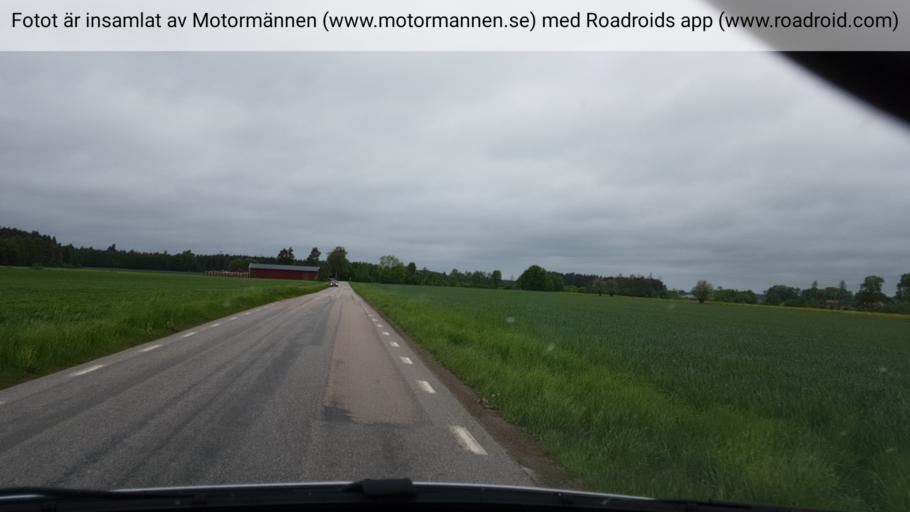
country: SE
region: Vaestra Goetaland
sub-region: Gotene Kommun
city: Kallby
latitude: 58.4759
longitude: 13.3232
